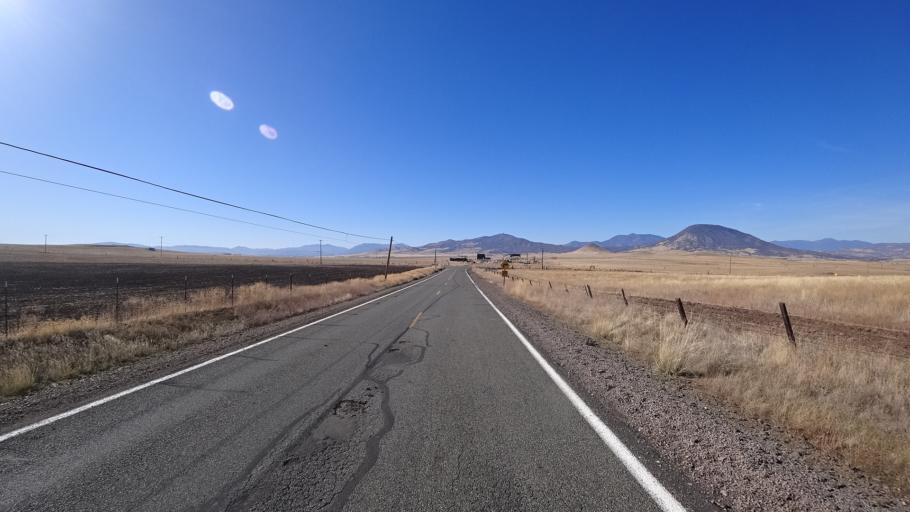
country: US
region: California
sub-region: Siskiyou County
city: Montague
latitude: 41.8042
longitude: -122.4135
